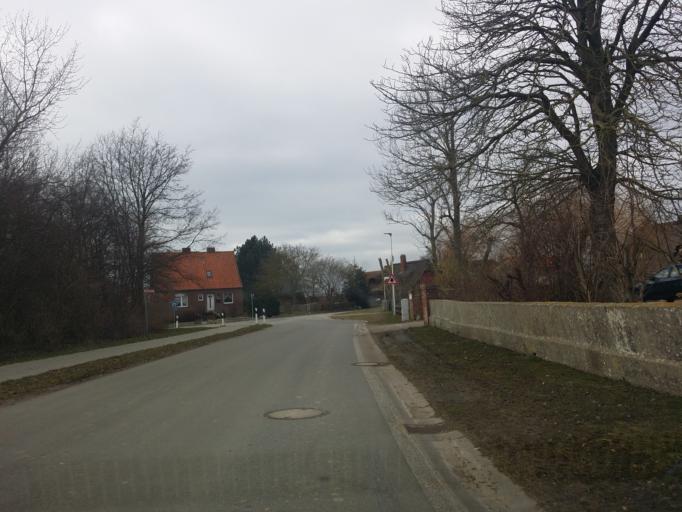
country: DE
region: Schleswig-Holstein
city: Grossenbrode
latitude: 54.4887
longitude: 11.0307
